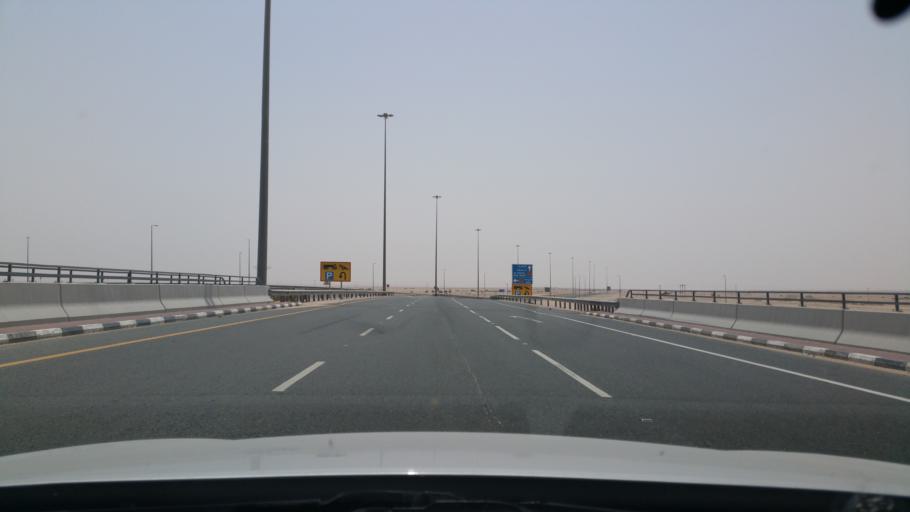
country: QA
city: Umm Bab
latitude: 24.9391
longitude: 50.9913
